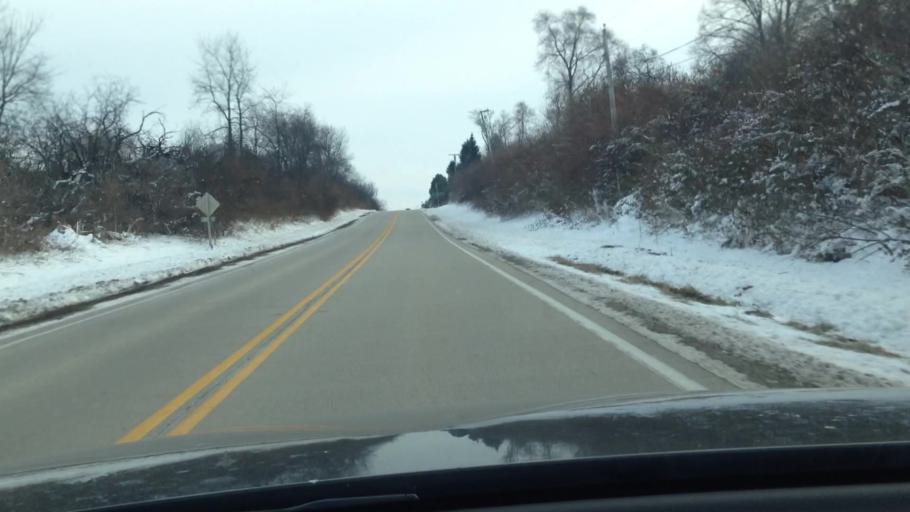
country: US
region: Illinois
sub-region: McHenry County
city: Woodstock
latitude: 42.3856
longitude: -88.4433
